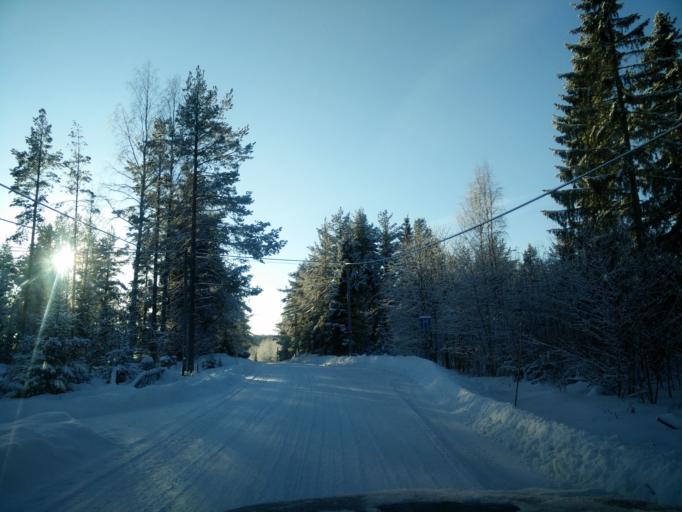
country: SE
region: Vaesternorrland
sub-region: Sundsvalls Kommun
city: Njurundabommen
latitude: 62.2283
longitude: 17.4991
